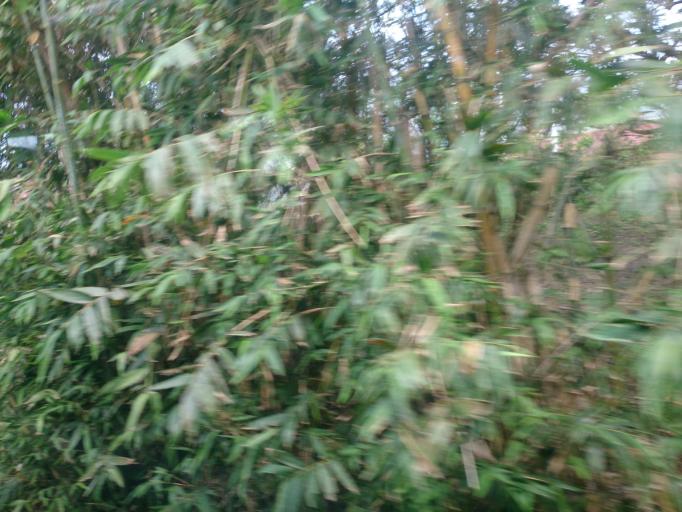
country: TW
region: Taipei
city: Taipei
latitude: 25.1551
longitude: 121.5466
